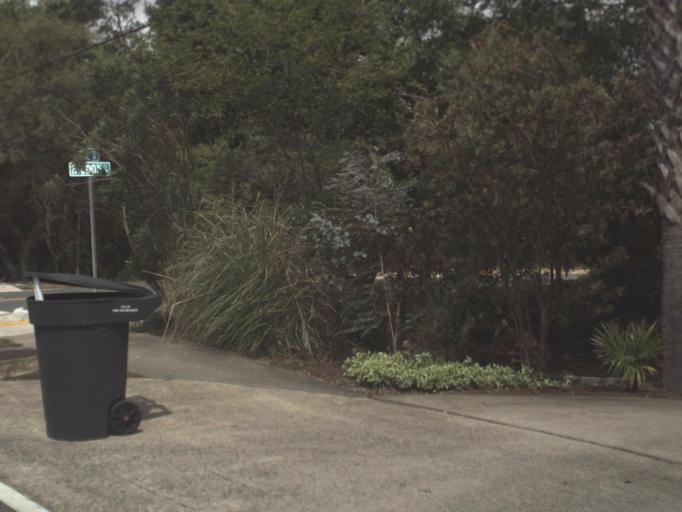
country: US
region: Florida
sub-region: Okaloosa County
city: Ocean City
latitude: 30.4273
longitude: -86.6256
